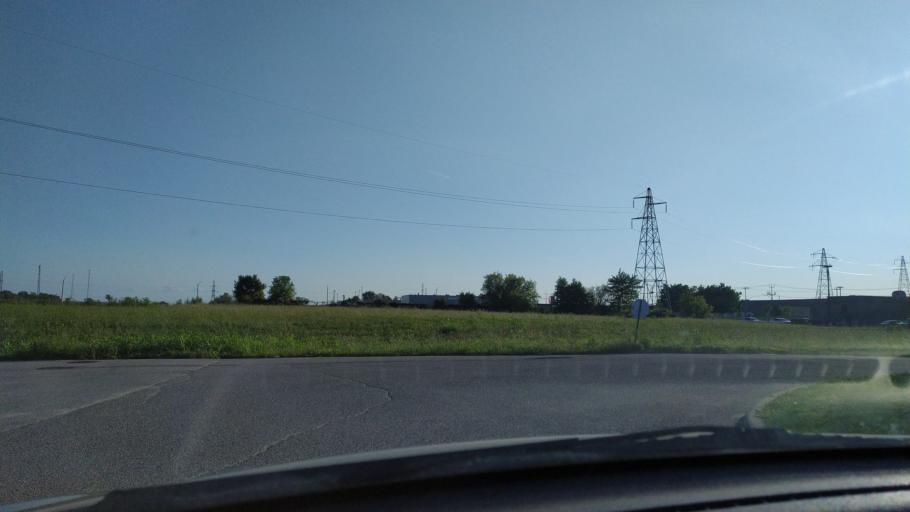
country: CA
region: Ontario
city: Stratford
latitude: 43.3525
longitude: -80.9967
